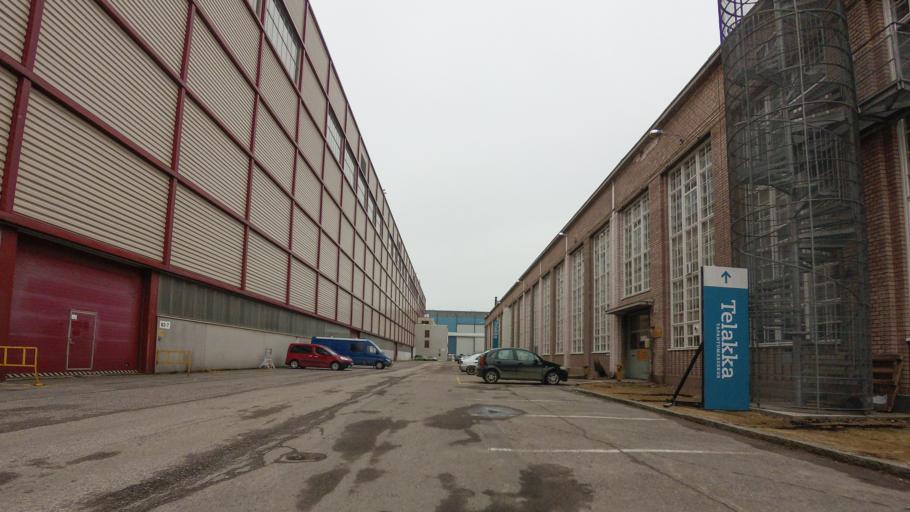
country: FI
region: Uusimaa
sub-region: Helsinki
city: Helsinki
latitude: 60.1524
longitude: 24.9258
